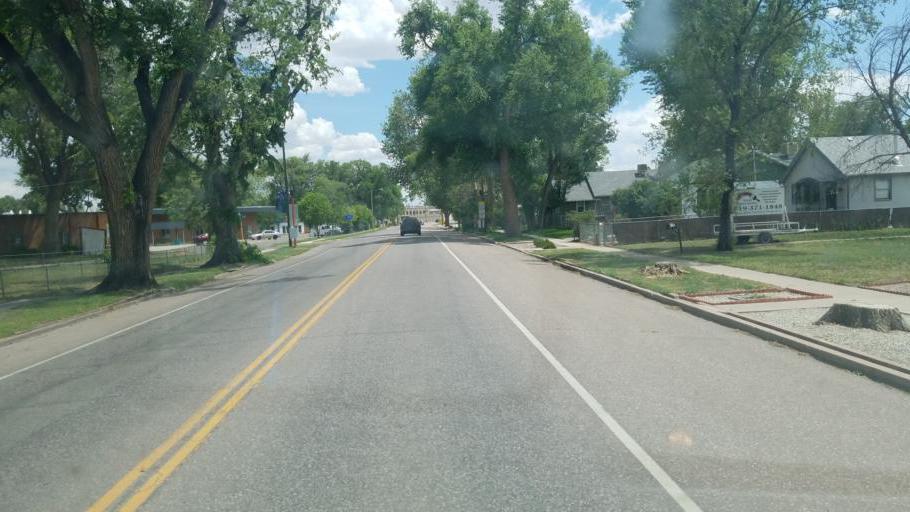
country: US
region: Colorado
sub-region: Fremont County
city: Florence
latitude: 38.3946
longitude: -105.1248
